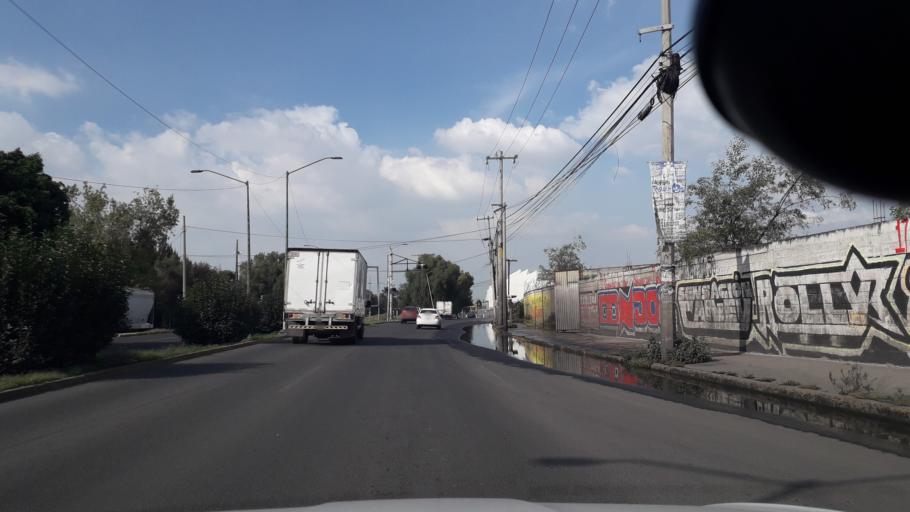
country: MX
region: Mexico
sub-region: Tultitlan
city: Buenavista
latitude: 19.6172
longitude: -99.1861
